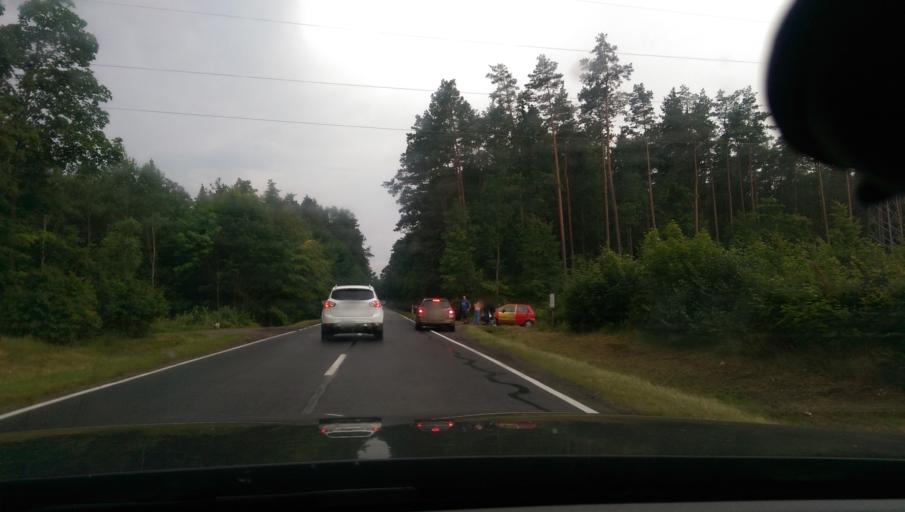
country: PL
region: Warmian-Masurian Voivodeship
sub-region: Powiat szczycienski
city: Szczytno
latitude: 53.5288
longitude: 20.9808
